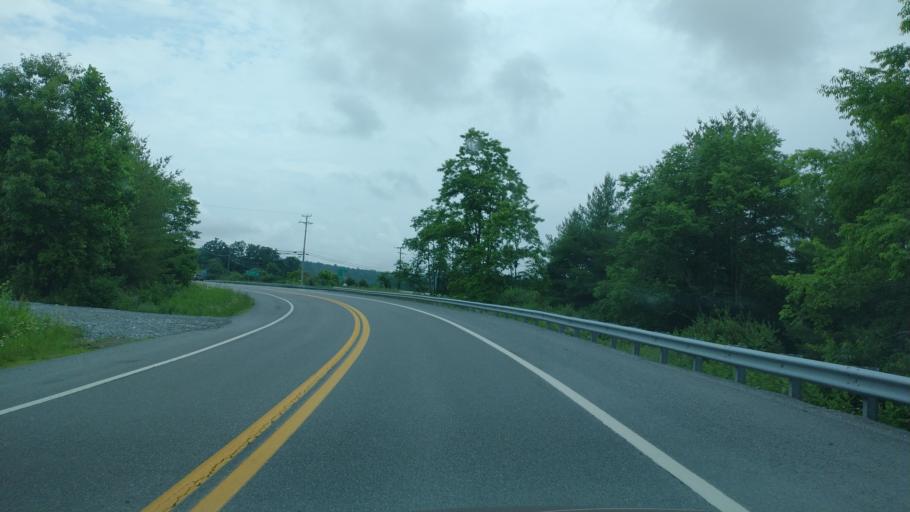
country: US
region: West Virginia
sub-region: Mercer County
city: Athens
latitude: 37.4250
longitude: -81.0620
